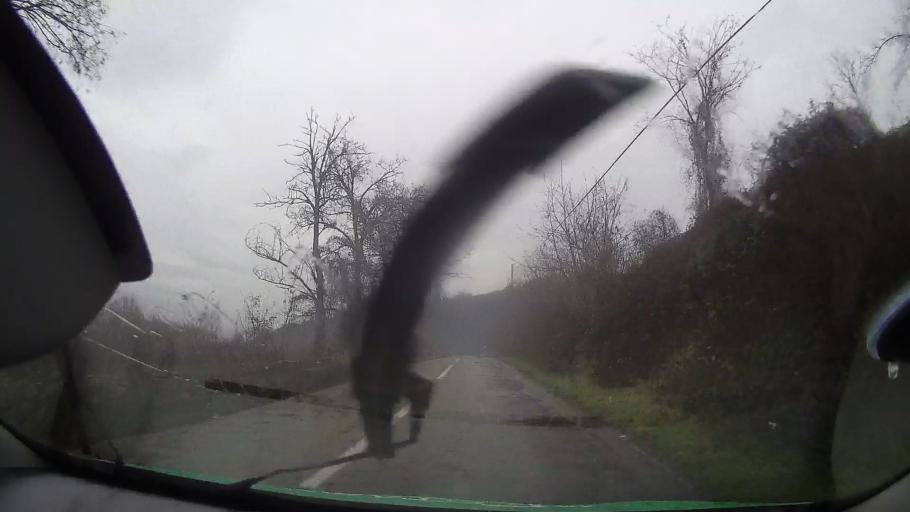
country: RO
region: Bihor
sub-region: Comuna Holod
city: Holod
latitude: 46.7739
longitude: 22.1360
